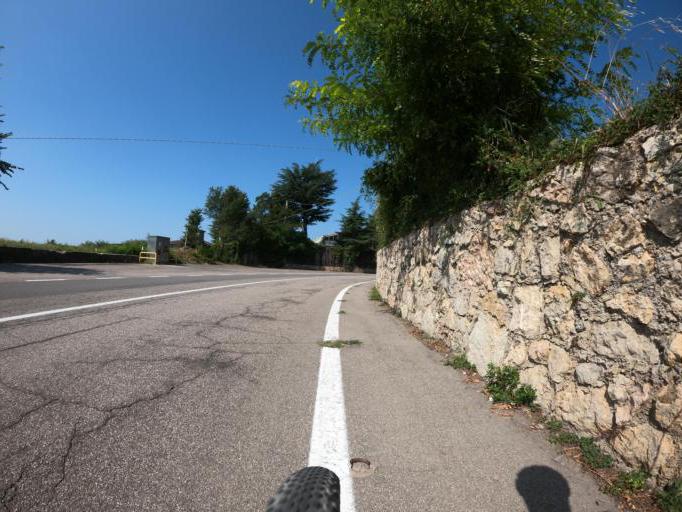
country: IT
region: Veneto
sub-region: Provincia di Verona
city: Caprino Veronese
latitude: 45.6092
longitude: 10.8122
